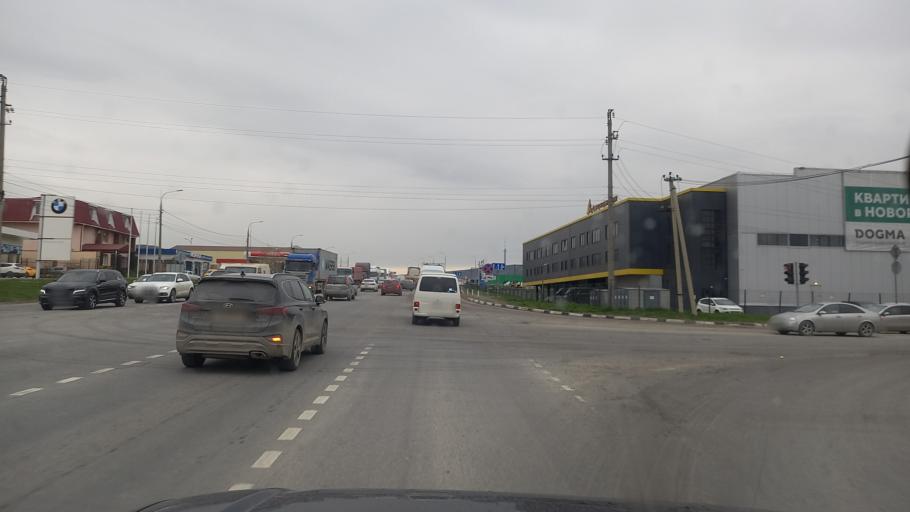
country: RU
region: Krasnodarskiy
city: Gayduk
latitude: 44.7719
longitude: 37.6962
